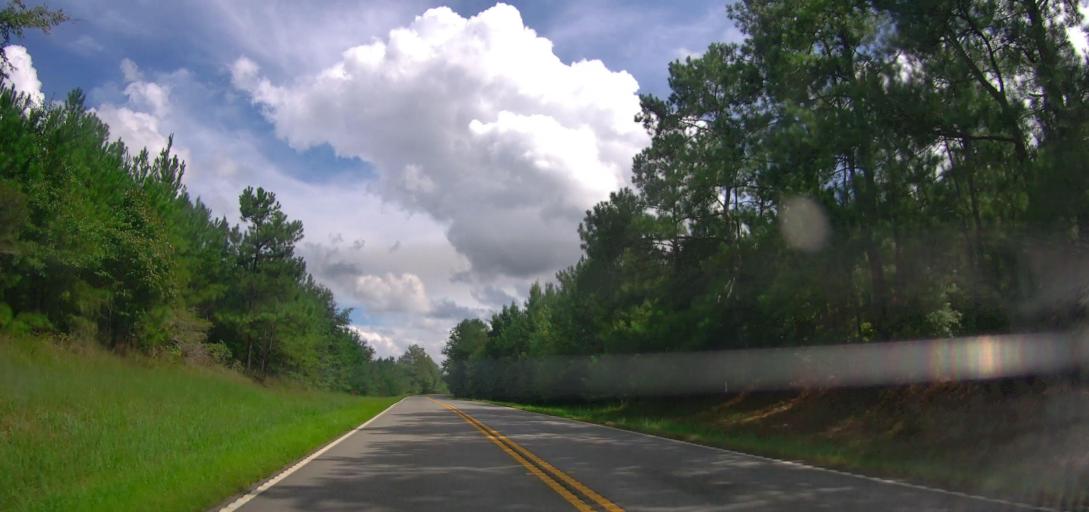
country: US
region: Georgia
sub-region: Talbot County
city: Talbotton
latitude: 32.6646
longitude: -84.5164
